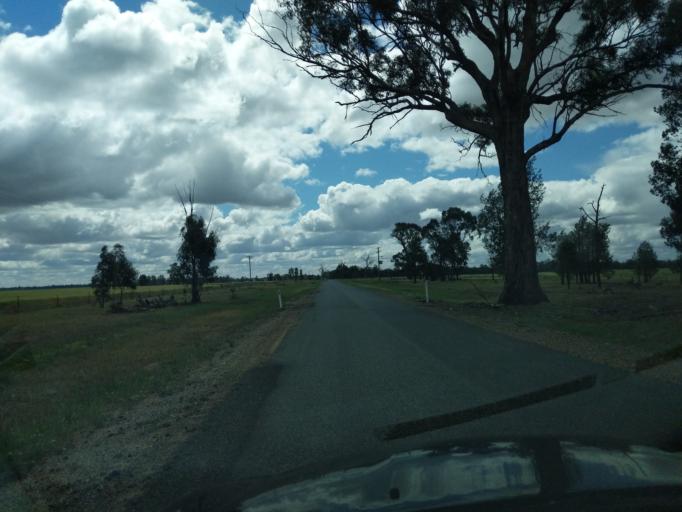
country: AU
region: New South Wales
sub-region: Coolamon
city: Coolamon
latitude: -34.8613
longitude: 146.8977
